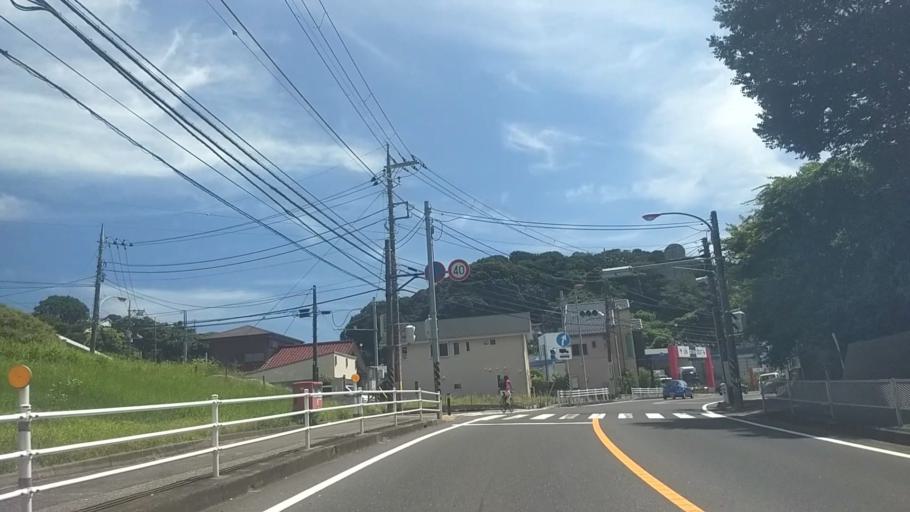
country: JP
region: Kanagawa
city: Yokosuka
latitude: 35.2526
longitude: 139.6656
